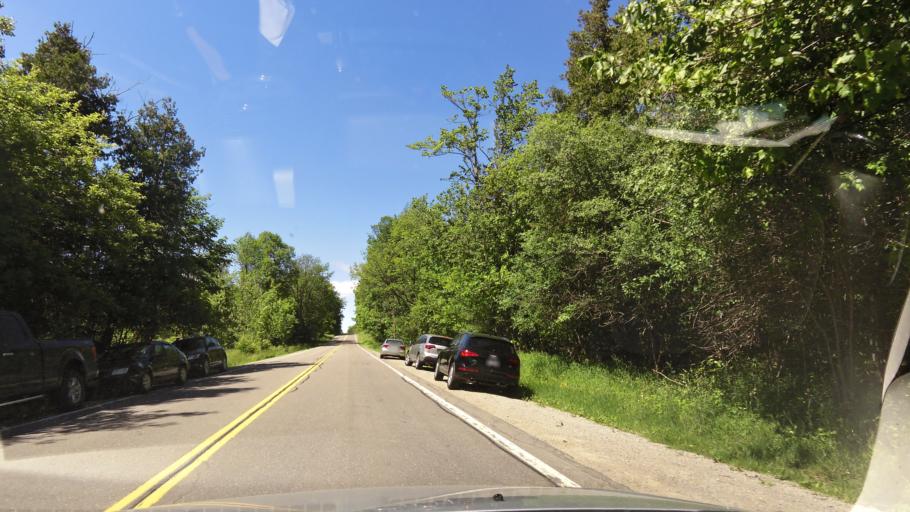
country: CA
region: Ontario
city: Newmarket
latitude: 43.9542
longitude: -79.5352
